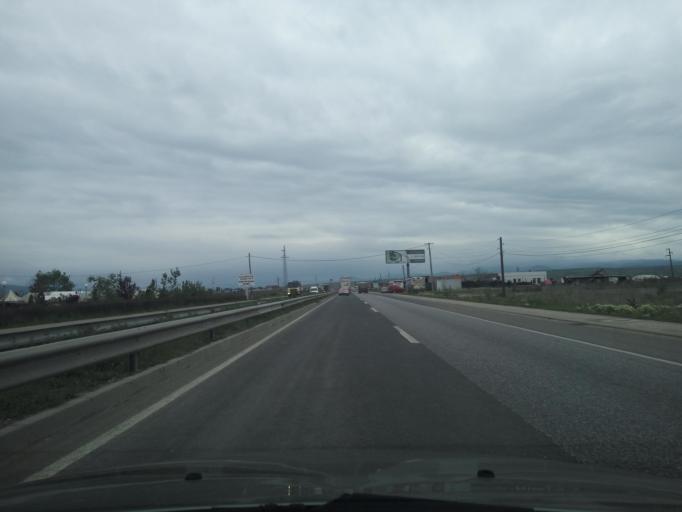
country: XK
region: Pristina
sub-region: Komuna e Obiliqit
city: Obiliq
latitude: 42.7116
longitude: 21.1006
